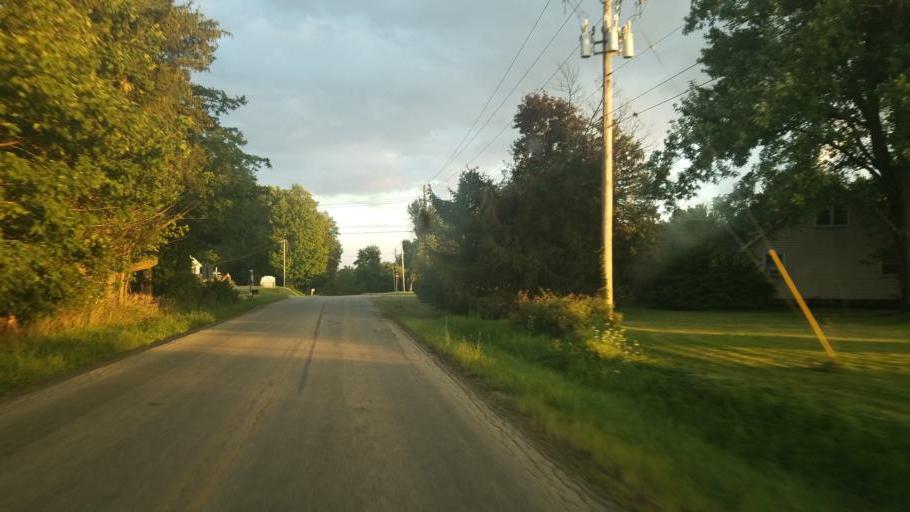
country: US
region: Ohio
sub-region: Richland County
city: Mansfield
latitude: 40.8066
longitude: -82.5395
